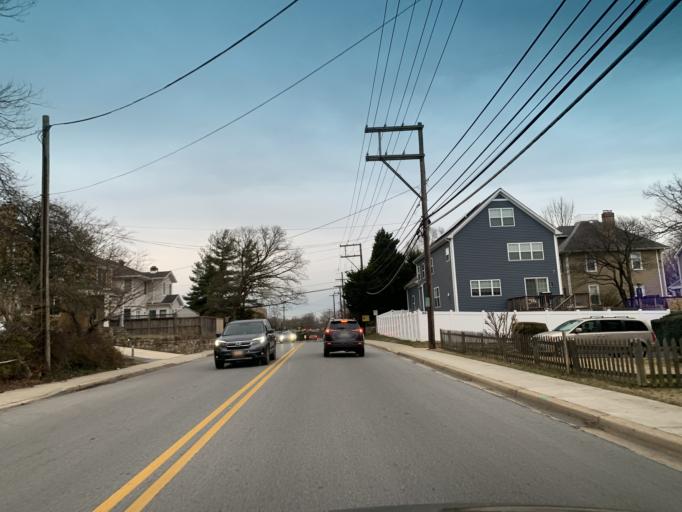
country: US
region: Maryland
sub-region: Montgomery County
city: North Kensington
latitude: 39.0356
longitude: -77.0726
